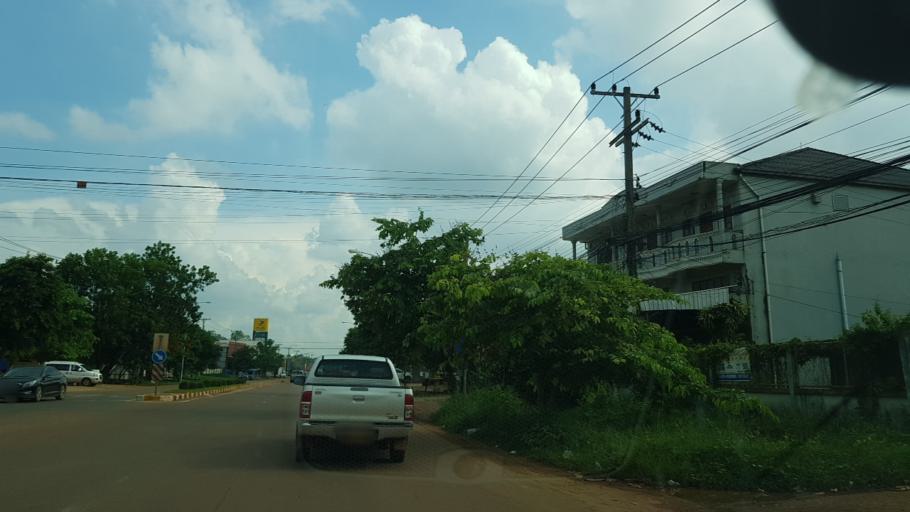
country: LA
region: Vientiane
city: Vientiane
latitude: 18.0199
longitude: 102.6510
